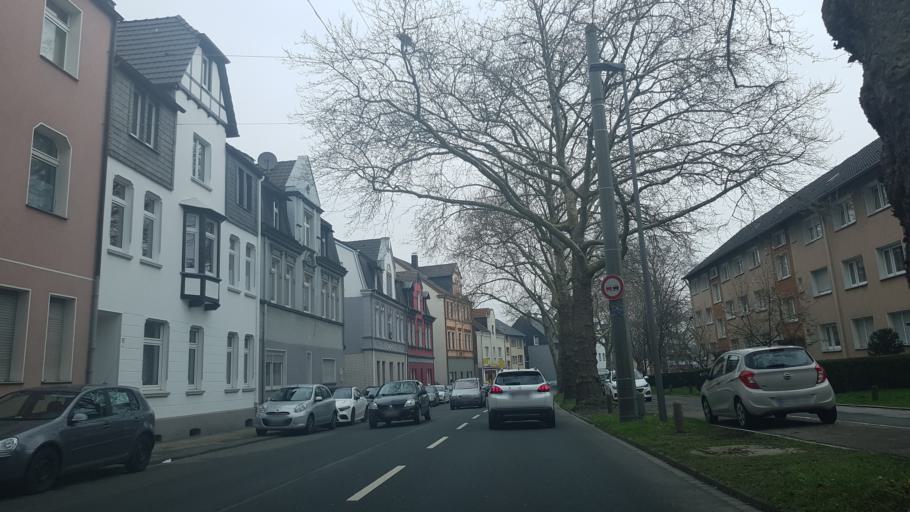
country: DE
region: North Rhine-Westphalia
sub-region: Regierungsbezirk Munster
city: Gelsenkirchen
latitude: 51.4863
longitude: 7.1351
